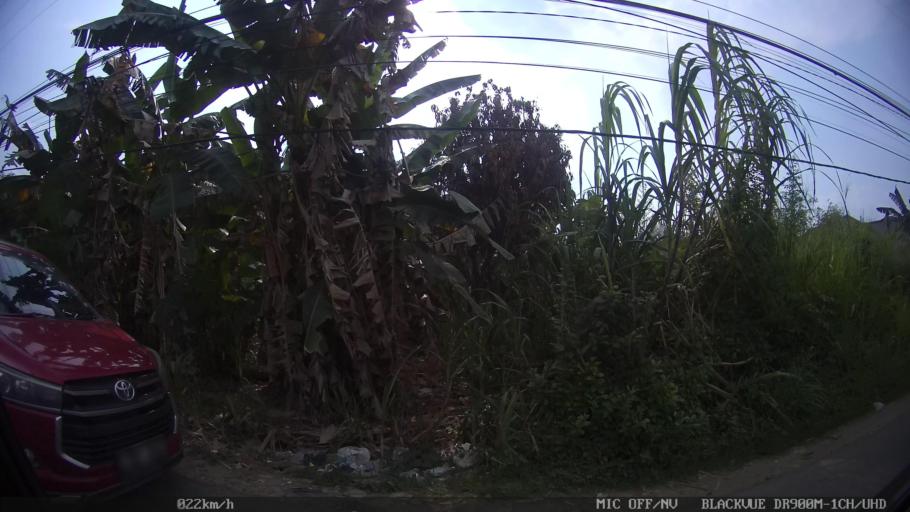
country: ID
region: Lampung
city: Kedaton
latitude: -5.3700
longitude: 105.2207
